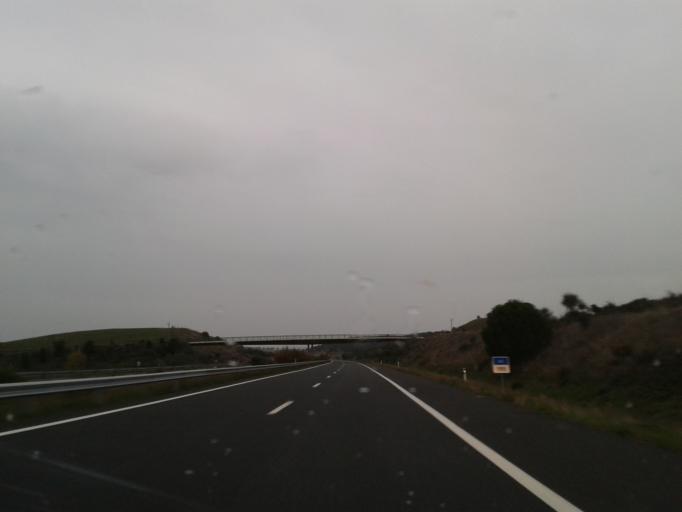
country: PT
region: Beja
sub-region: Aljustrel
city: Aljustrel
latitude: 37.8607
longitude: -8.2300
